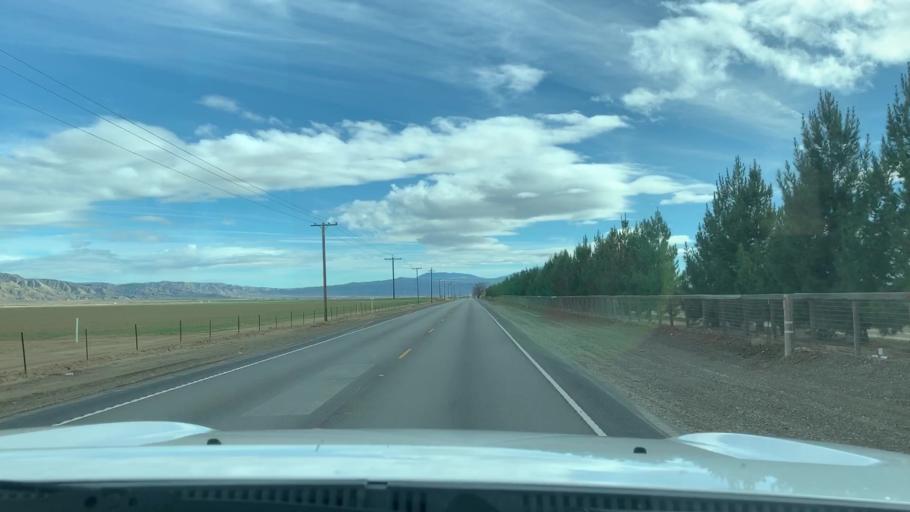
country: US
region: California
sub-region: Kern County
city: Taft Heights
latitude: 34.9425
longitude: -119.6591
